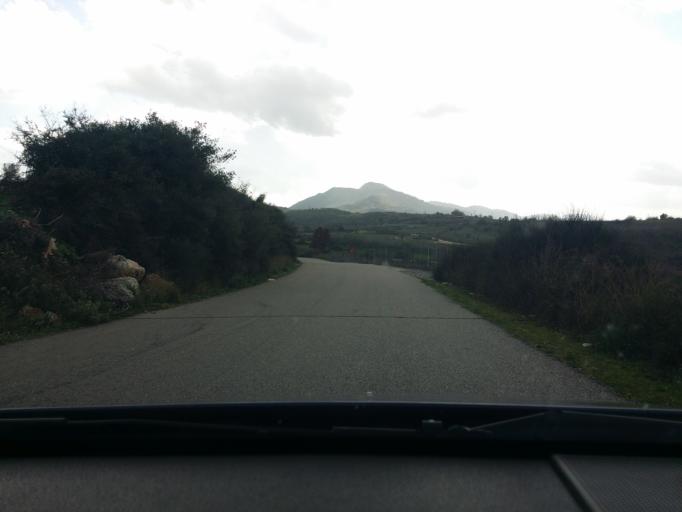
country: GR
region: West Greece
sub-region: Nomos Aitolias kai Akarnanias
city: Fitiai
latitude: 38.6901
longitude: 21.1785
